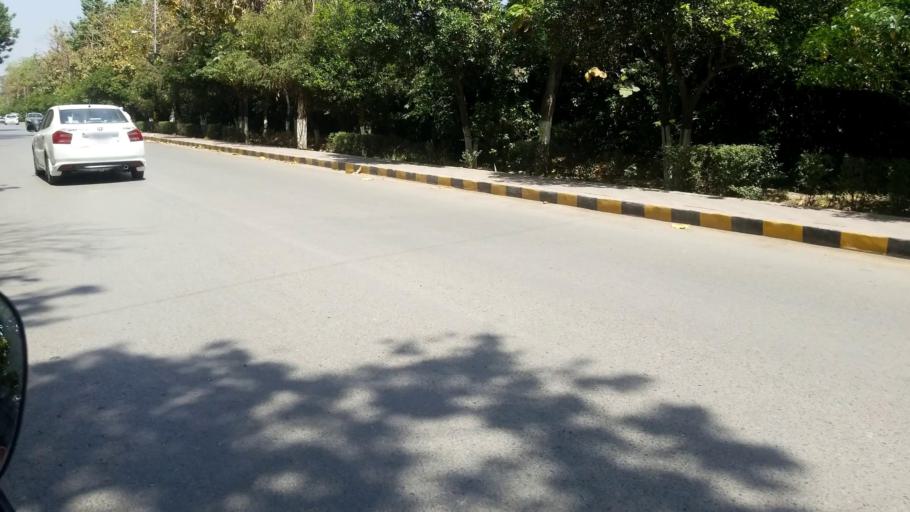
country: PK
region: Khyber Pakhtunkhwa
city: Peshawar
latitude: 34.0011
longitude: 71.4862
